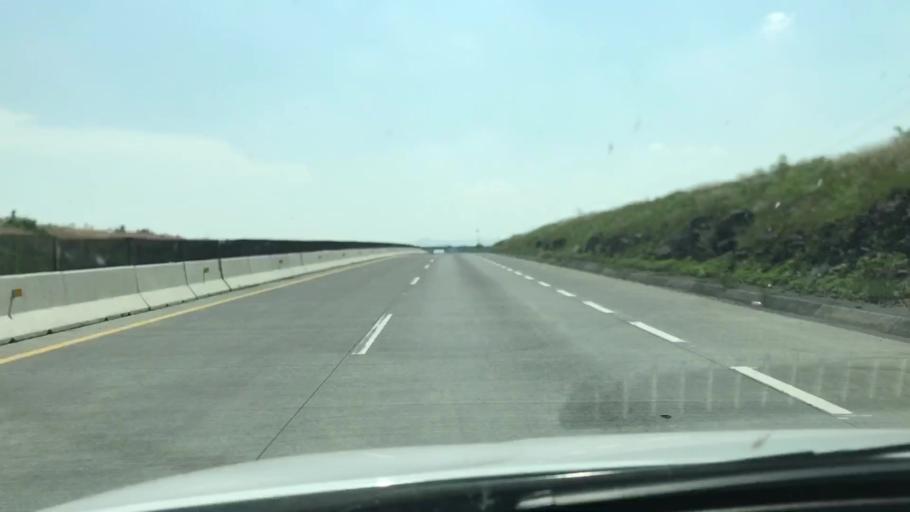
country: MX
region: Michoacan
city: La Piedad Cavadas
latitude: 20.3913
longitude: -102.0988
